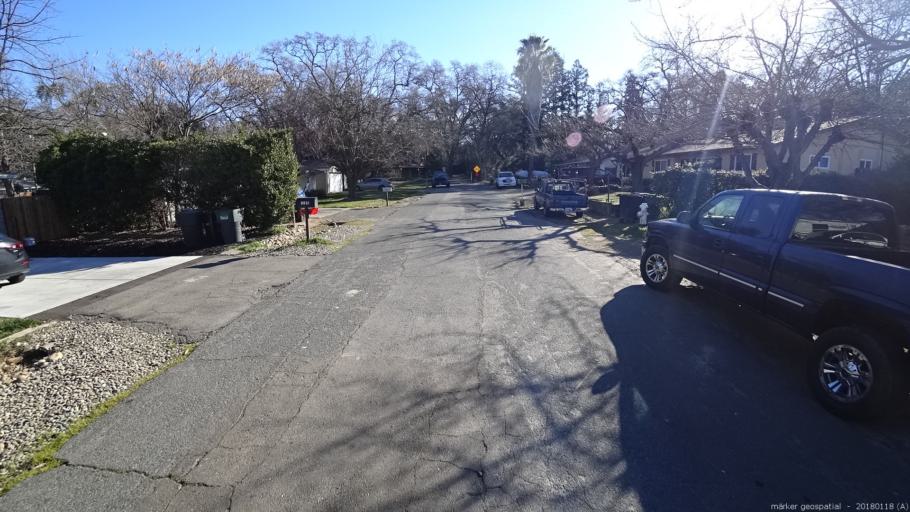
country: US
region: California
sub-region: Sacramento County
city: Orangevale
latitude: 38.6706
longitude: -121.2381
